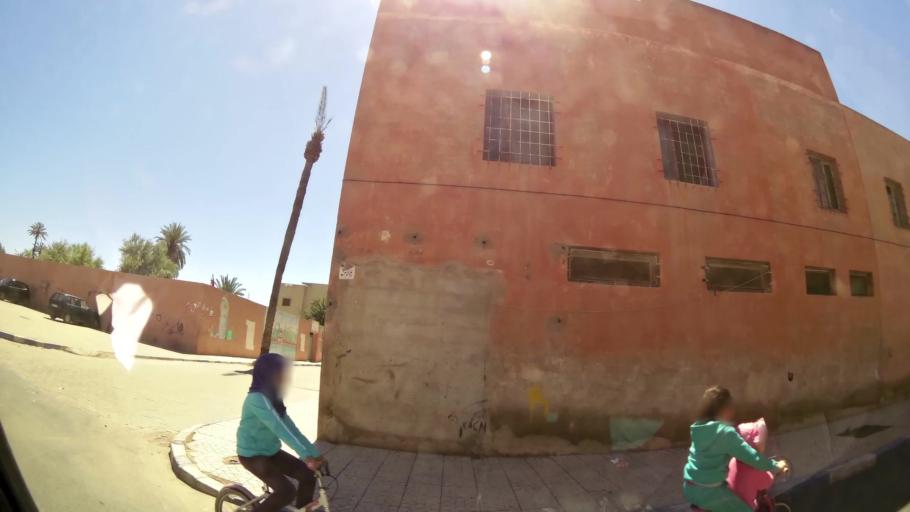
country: MA
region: Marrakech-Tensift-Al Haouz
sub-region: Marrakech
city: Marrakesh
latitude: 31.6496
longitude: -7.9915
